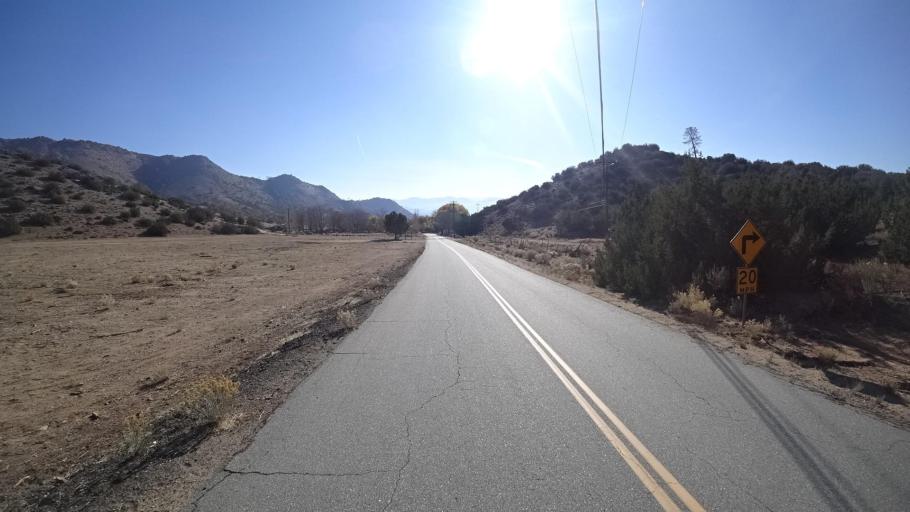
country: US
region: California
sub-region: Kern County
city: Tehachapi
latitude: 35.3658
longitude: -118.3845
